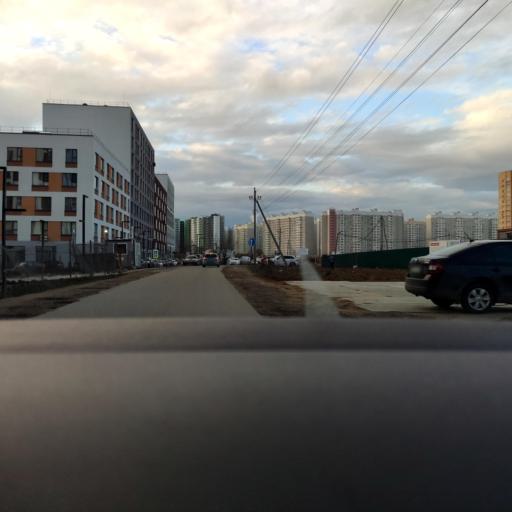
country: RU
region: Moskovskaya
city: Vidnoye
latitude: 55.5337
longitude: 37.7167
